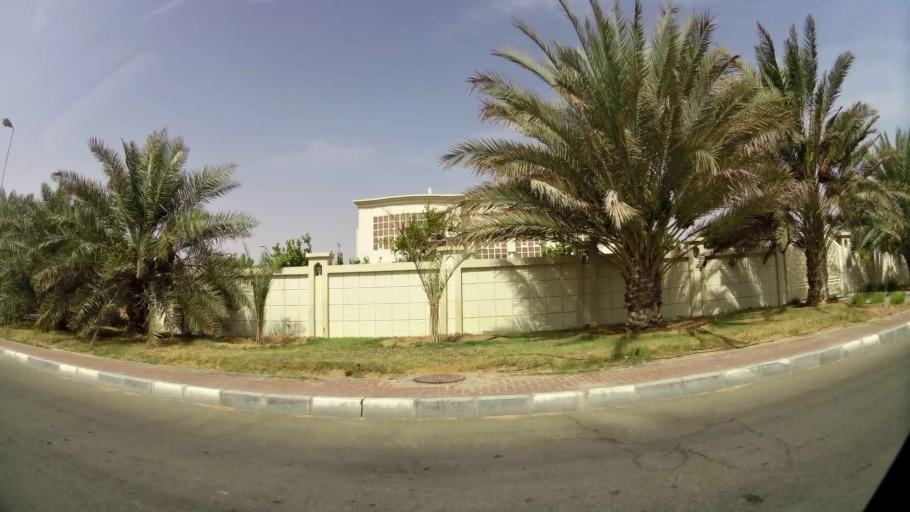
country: AE
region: Abu Dhabi
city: Al Ain
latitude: 24.1661
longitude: 55.6814
